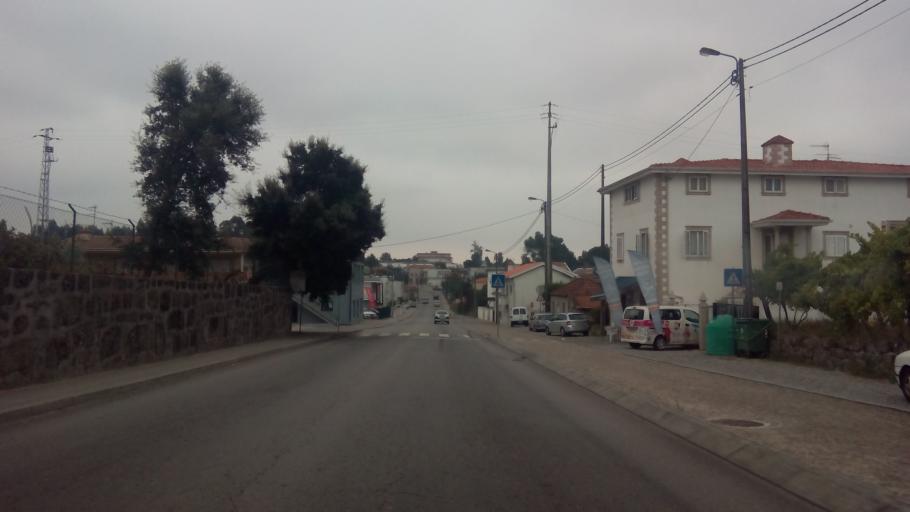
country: PT
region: Porto
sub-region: Paredes
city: Madalena
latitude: 41.2135
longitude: -8.3454
